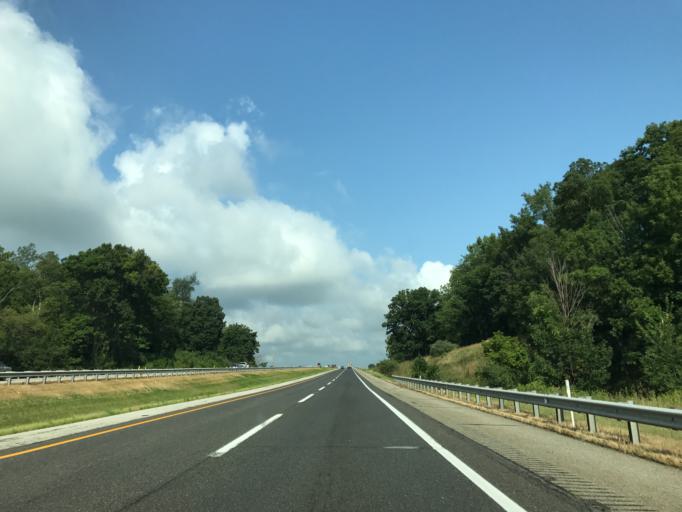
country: US
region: Indiana
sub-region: Steuben County
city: Fremont
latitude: 41.7086
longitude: -84.9351
